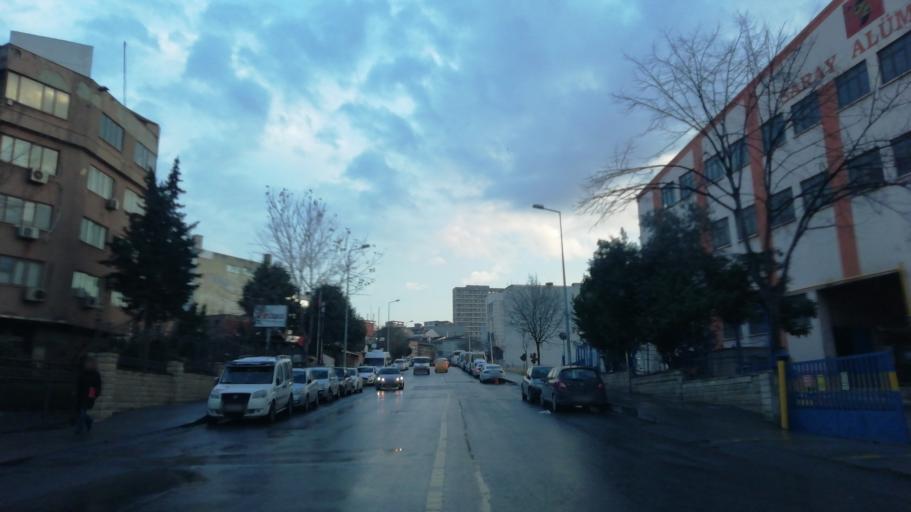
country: TR
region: Istanbul
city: Mahmutbey
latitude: 41.0252
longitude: 28.8182
